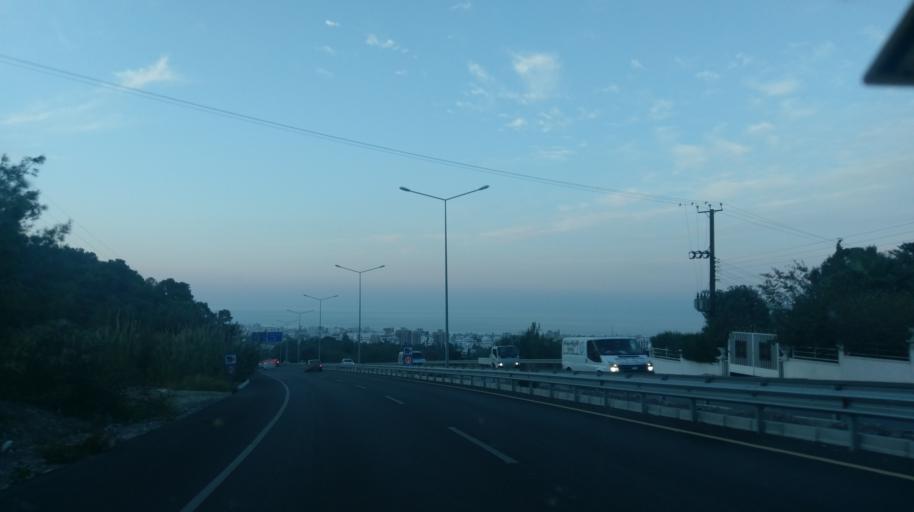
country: CY
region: Keryneia
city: Kyrenia
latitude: 35.3186
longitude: 33.3217
